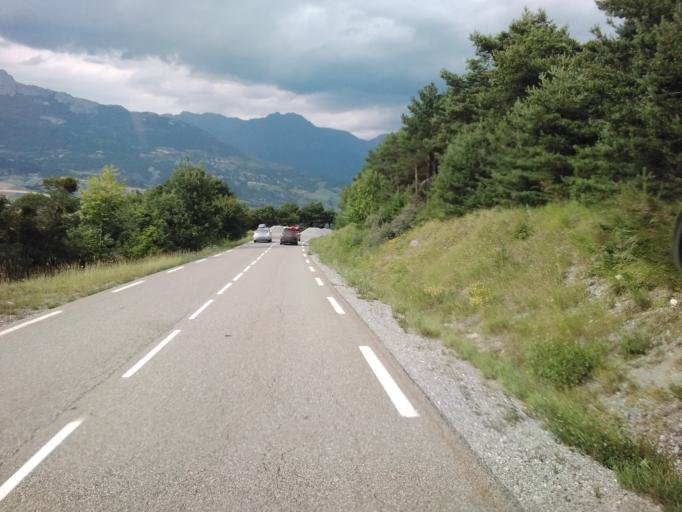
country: FR
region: Provence-Alpes-Cote d'Azur
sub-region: Departement des Hautes-Alpes
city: Chorges
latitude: 44.5077
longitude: 6.3517
